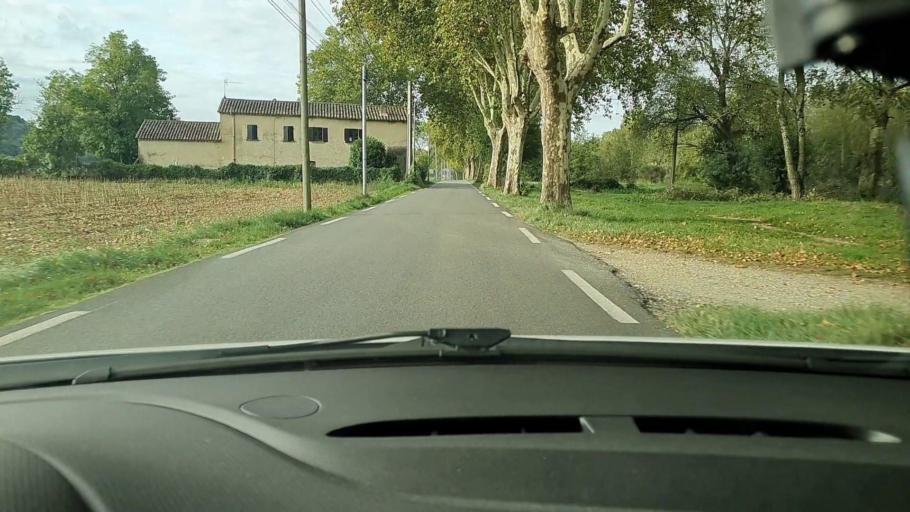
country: FR
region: Languedoc-Roussillon
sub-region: Departement du Gard
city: Saint-Ambroix
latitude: 44.1937
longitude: 4.2406
